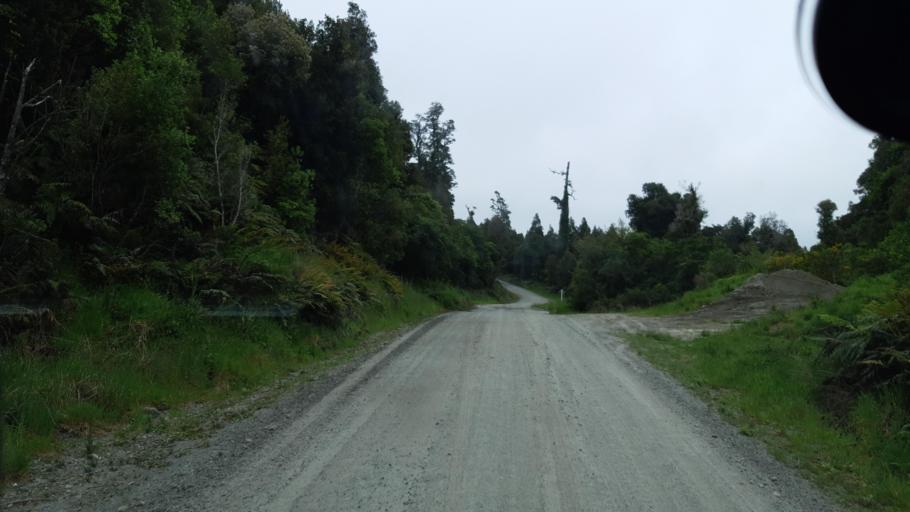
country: NZ
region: West Coast
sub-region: Grey District
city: Greymouth
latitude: -42.6414
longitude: 171.3759
